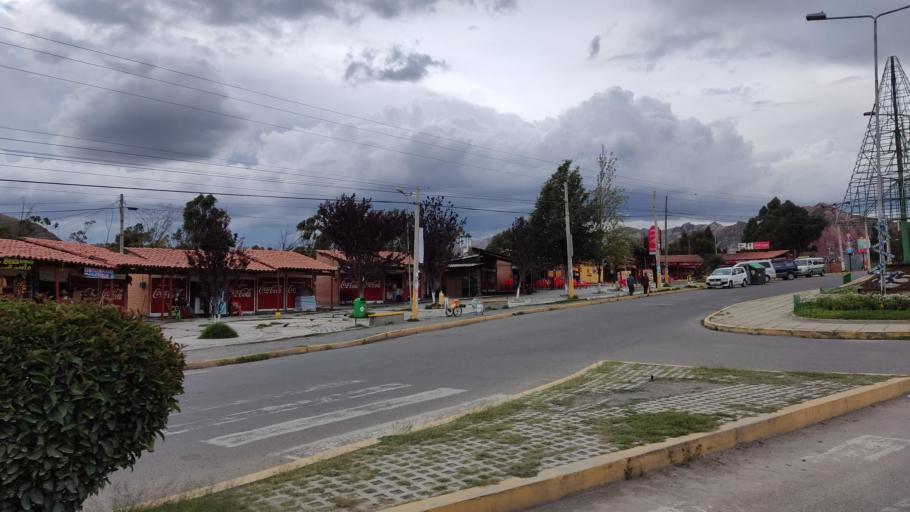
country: BO
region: La Paz
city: La Paz
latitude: -16.5722
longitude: -68.0833
